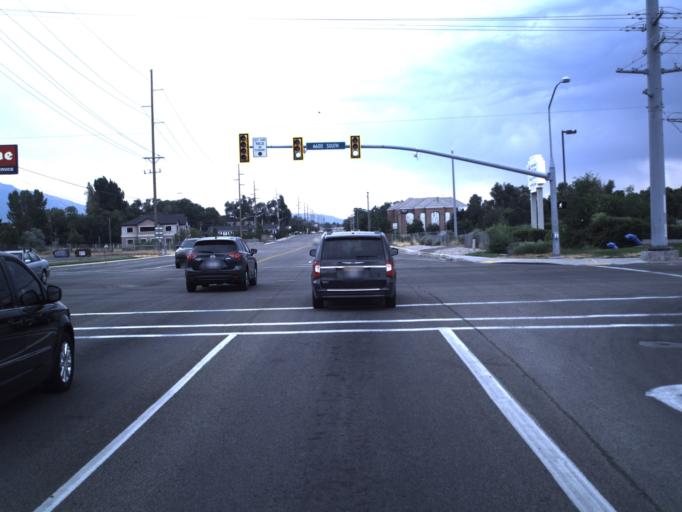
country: US
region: Utah
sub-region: Salt Lake County
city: Midvale
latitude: 40.6319
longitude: -111.8661
